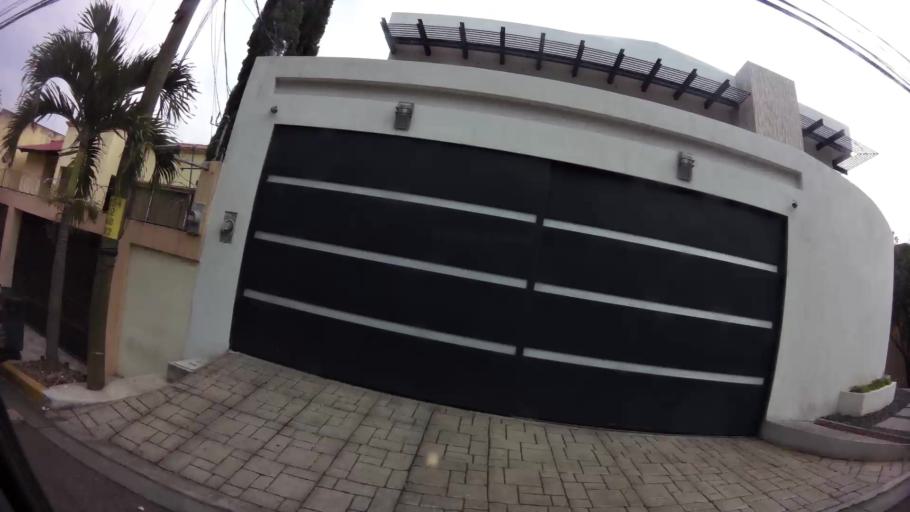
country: HN
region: Francisco Morazan
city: Tegucigalpa
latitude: 14.0925
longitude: -87.1765
